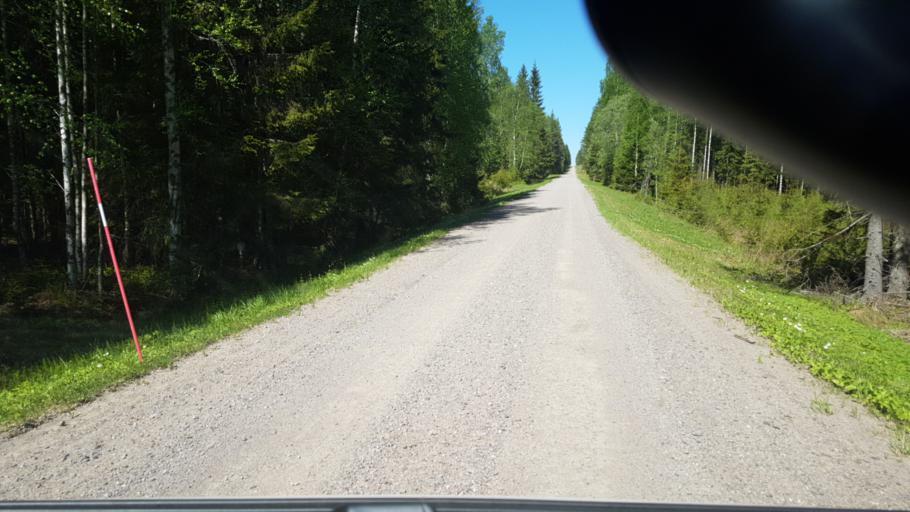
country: SE
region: Vaermland
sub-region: Eda Kommun
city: Charlottenberg
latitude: 60.0030
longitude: 12.5074
